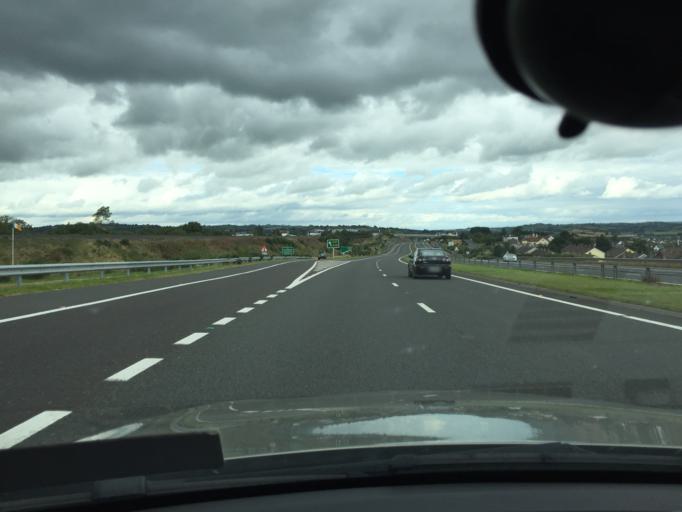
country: GB
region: Northern Ireland
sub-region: Newry and Mourne District
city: Newry
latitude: 54.1814
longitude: -6.3603
